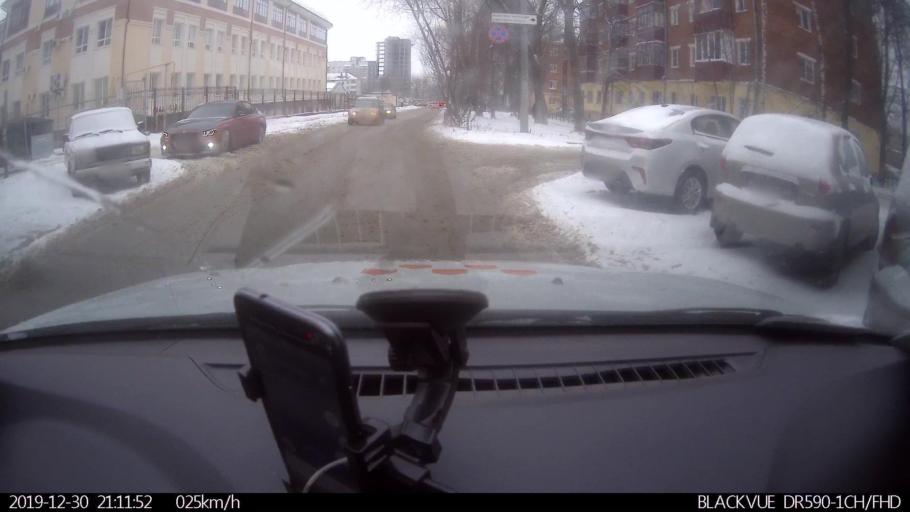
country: RU
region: Nizjnij Novgorod
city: Nizhniy Novgorod
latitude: 56.3115
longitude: 44.0290
